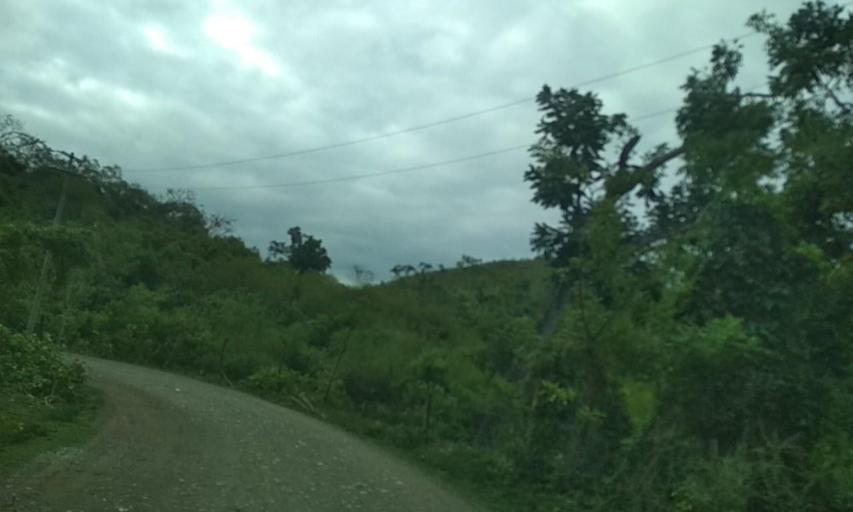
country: MX
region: Veracruz
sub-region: Papantla
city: Residencial Tajin
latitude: 20.6128
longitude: -97.3602
